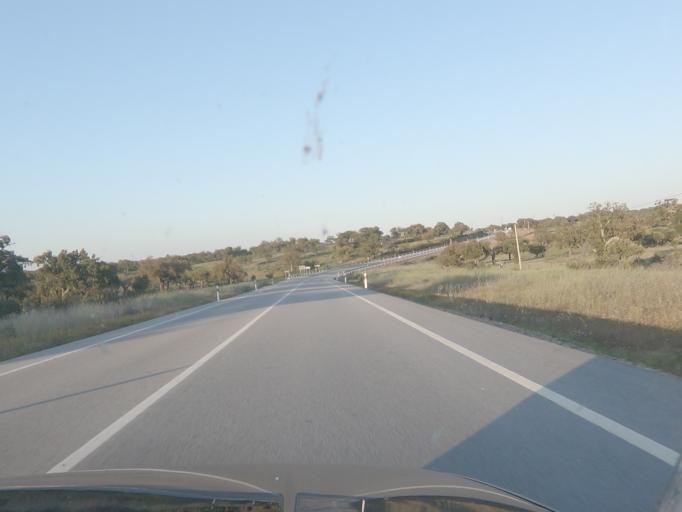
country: ES
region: Extremadura
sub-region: Provincia de Caceres
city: Carbajo
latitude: 39.5045
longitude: -7.1625
